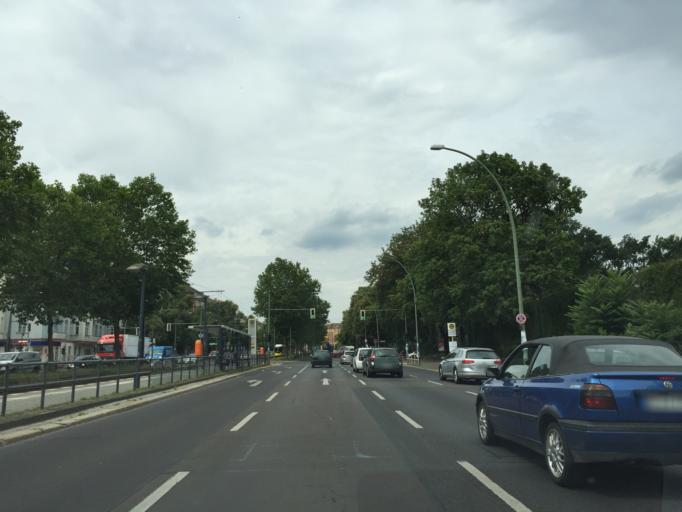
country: DE
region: Berlin
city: Prenzlauer Berg Bezirk
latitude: 52.5373
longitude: 13.4300
